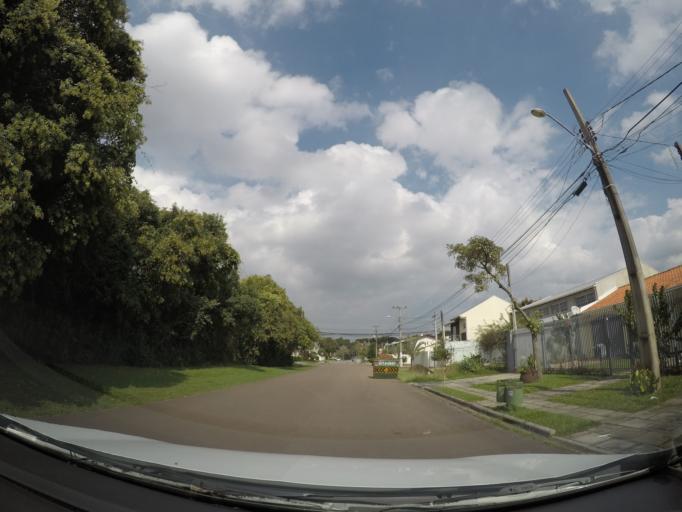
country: BR
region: Parana
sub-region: Curitiba
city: Curitiba
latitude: -25.4862
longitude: -49.2618
